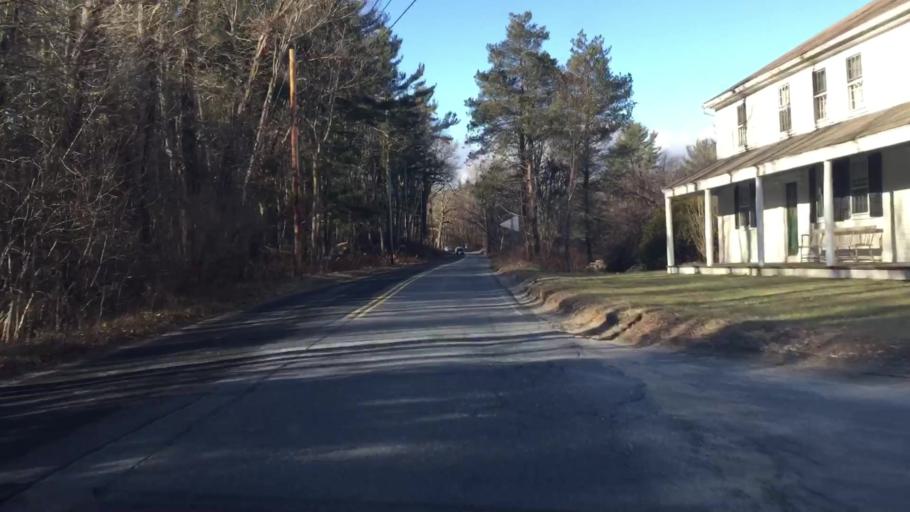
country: US
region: Massachusetts
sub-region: Worcester County
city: Sterling
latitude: 42.4372
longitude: -71.8195
